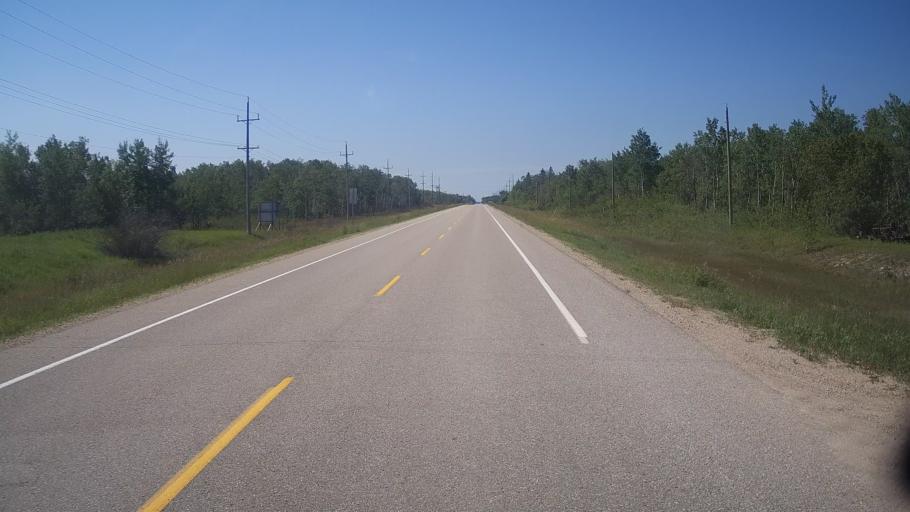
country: CA
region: Manitoba
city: La Broquerie
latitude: 49.6750
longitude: -96.4569
